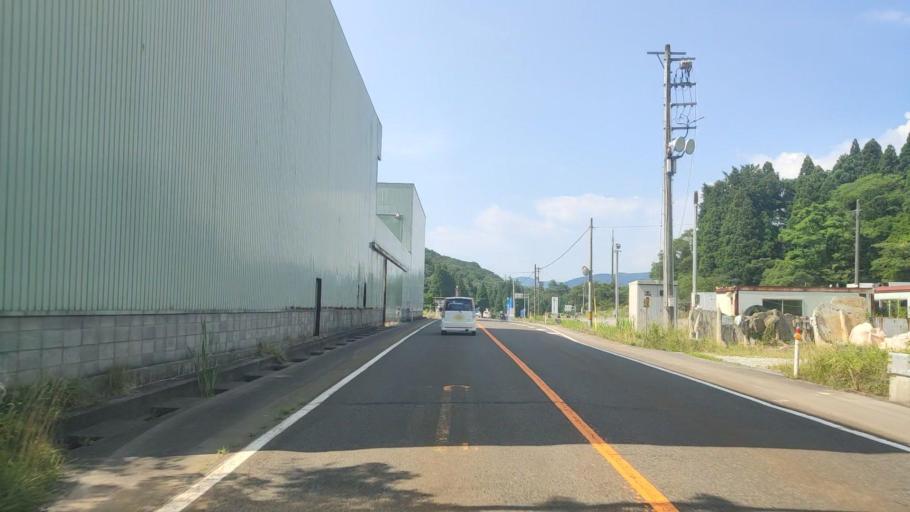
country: JP
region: Fukui
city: Tsuruga
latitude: 35.5762
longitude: 136.1227
